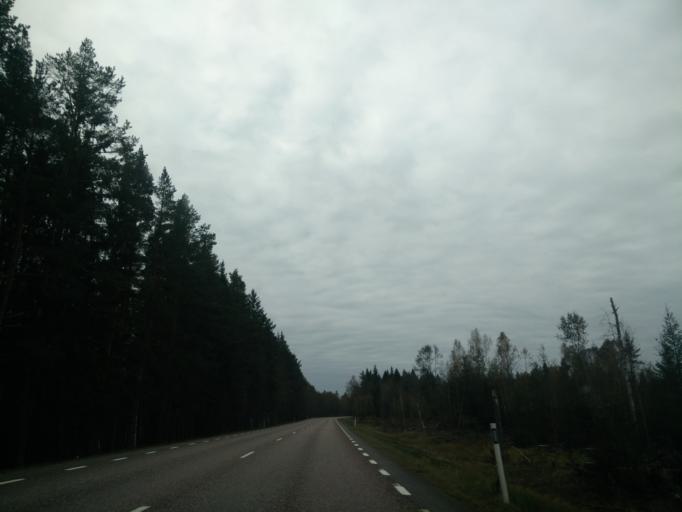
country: SE
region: Gaevleborg
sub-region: Gavle Kommun
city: Norrsundet
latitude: 60.8606
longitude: 17.1808
